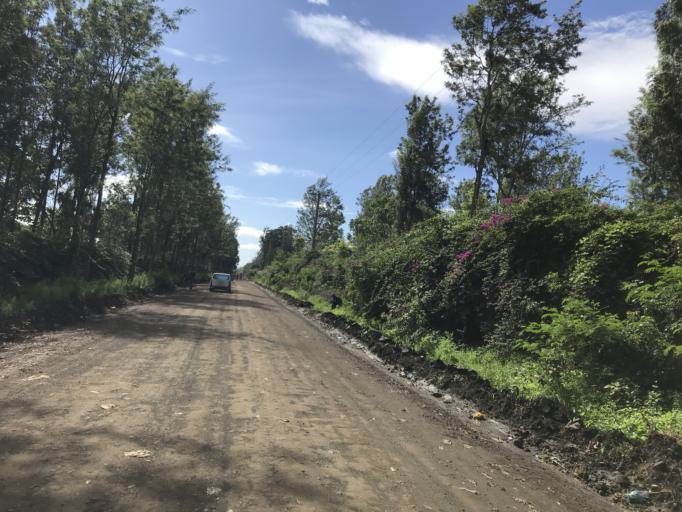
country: TZ
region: Arusha
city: Nkoaranga
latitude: -3.3759
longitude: 36.7884
